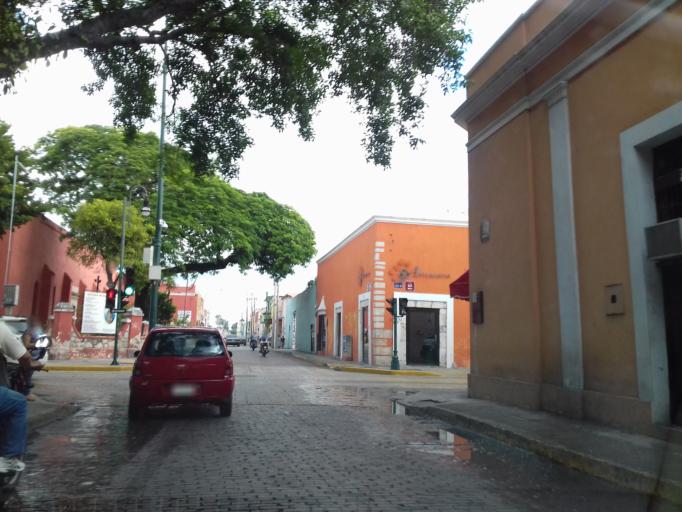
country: MX
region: Yucatan
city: Merida
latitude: 20.9710
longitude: -89.6226
